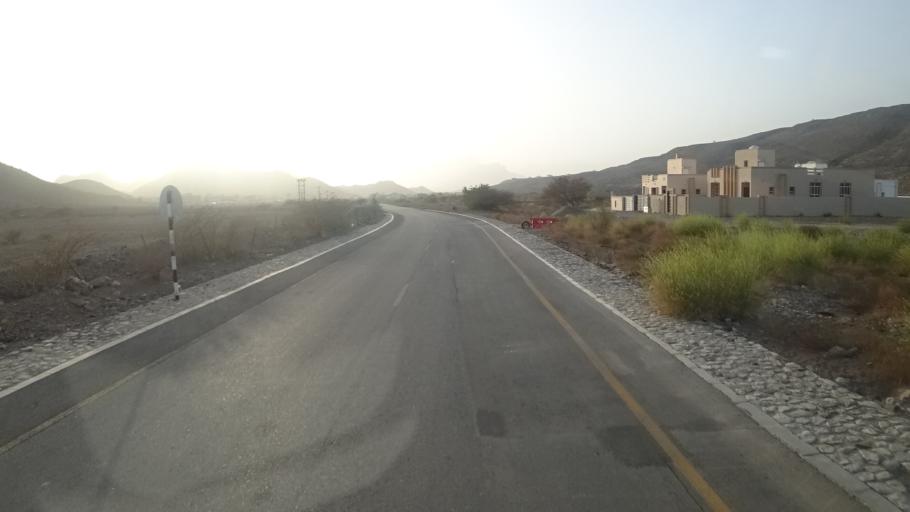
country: OM
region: Muhafazat ad Dakhiliyah
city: Bahla'
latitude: 23.0788
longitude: 57.3474
